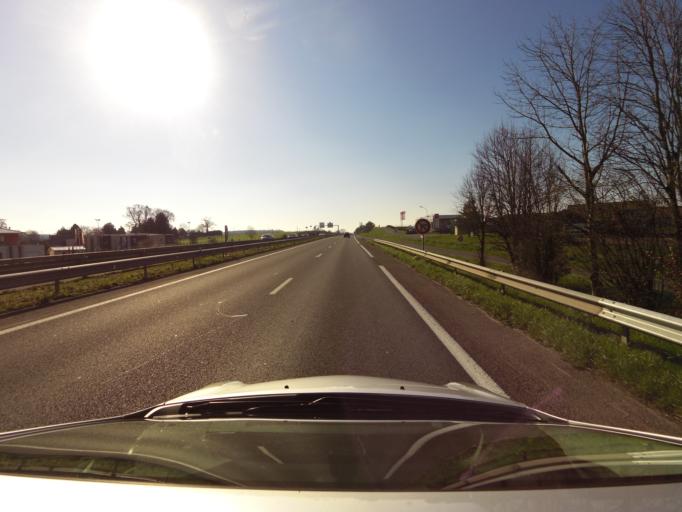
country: FR
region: Lower Normandy
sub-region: Departement de la Manche
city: Saint-Martin-des-Champs
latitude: 48.6494
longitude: -1.3501
